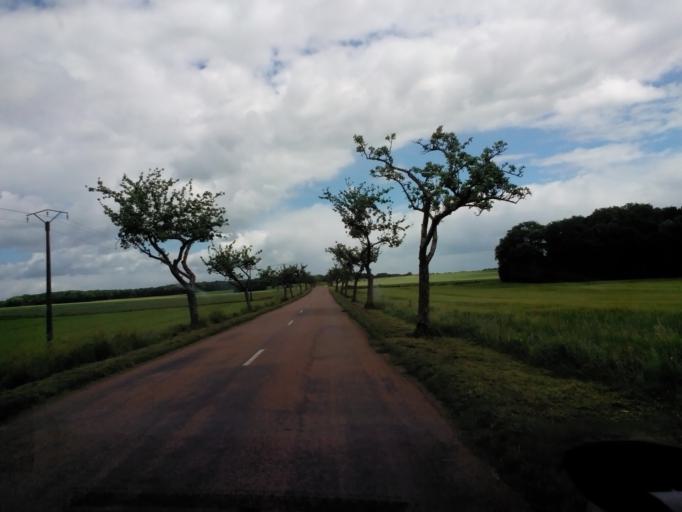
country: FR
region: Champagne-Ardenne
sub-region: Departement de la Haute-Marne
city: Rolampont
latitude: 47.9056
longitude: 5.2575
